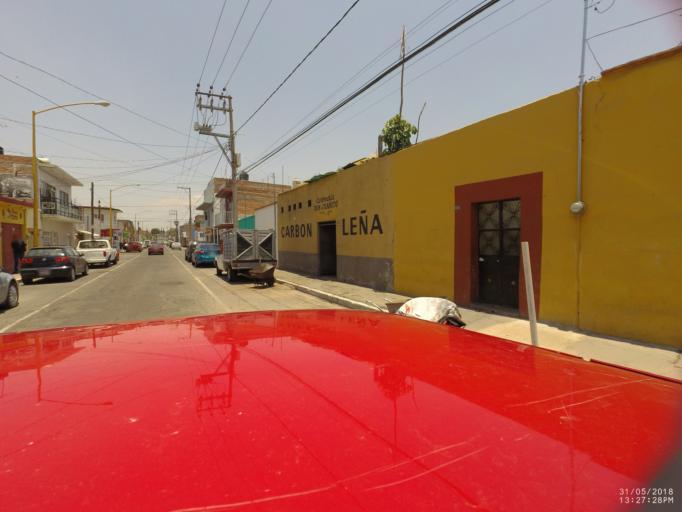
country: MX
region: Aguascalientes
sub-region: Aguascalientes
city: Aguascalientes
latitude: 21.8801
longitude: -102.3103
